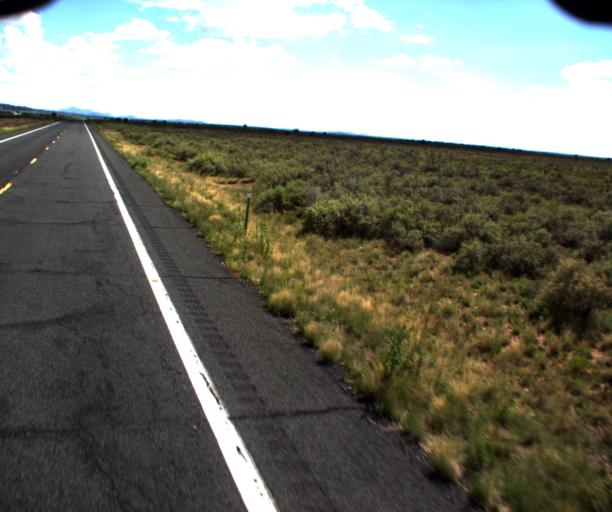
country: US
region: Arizona
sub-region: Coconino County
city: Williams
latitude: 35.6118
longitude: -112.1450
